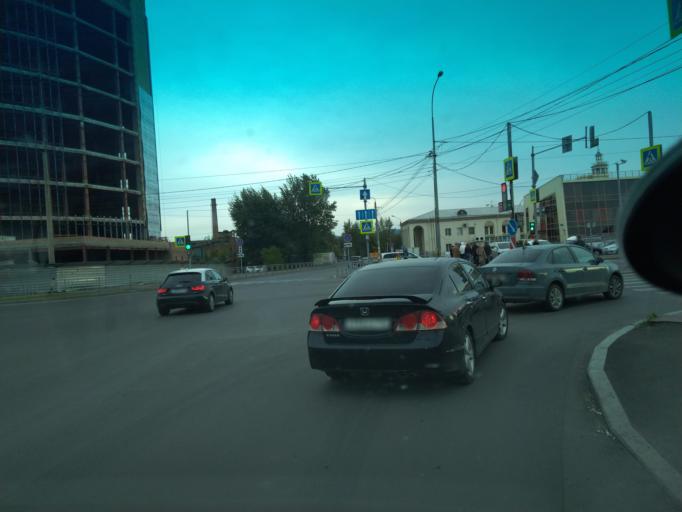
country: RU
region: Krasnoyarskiy
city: Krasnoyarsk
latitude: 56.0340
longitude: 92.9088
